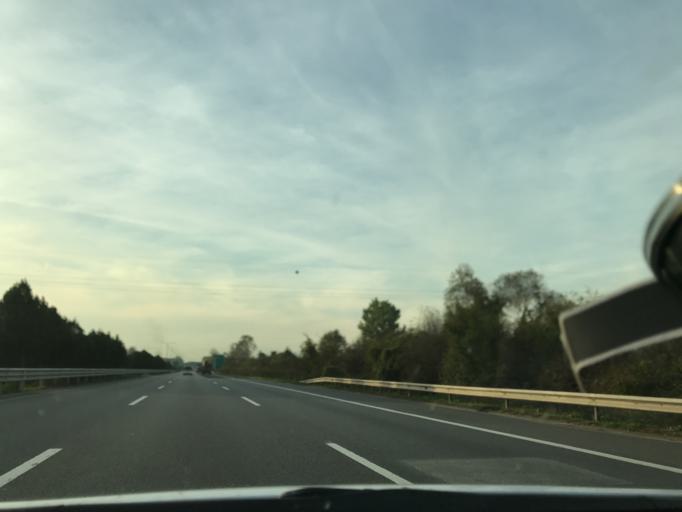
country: TR
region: Duzce
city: Cilimli
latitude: 40.8267
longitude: 31.0541
